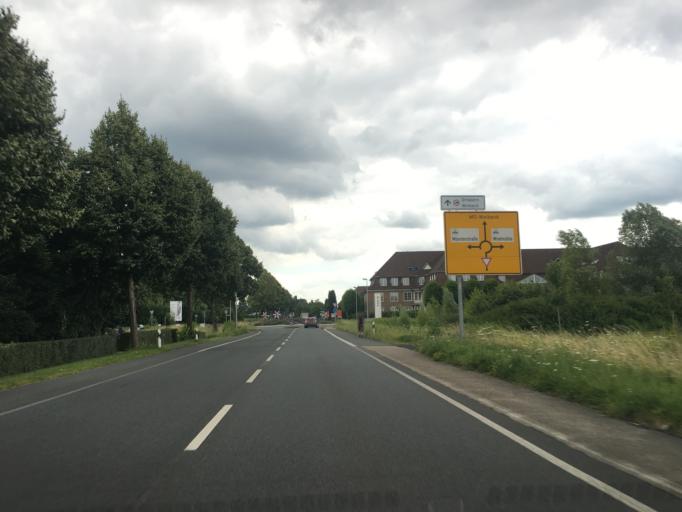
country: DE
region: North Rhine-Westphalia
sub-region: Regierungsbezirk Munster
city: Telgte
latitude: 51.9315
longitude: 7.7192
